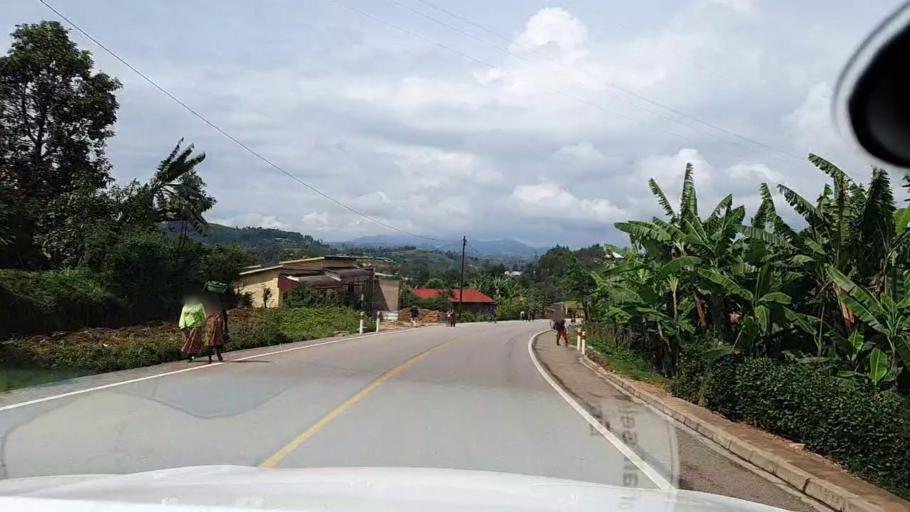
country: RW
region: Southern Province
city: Nzega
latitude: -2.4852
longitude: 29.5176
